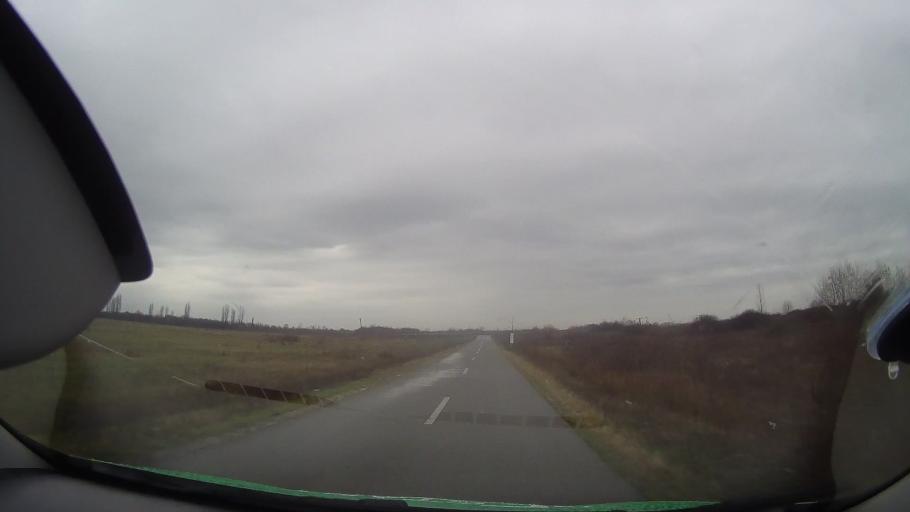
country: RO
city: Capalna
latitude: 46.7415
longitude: 22.1182
